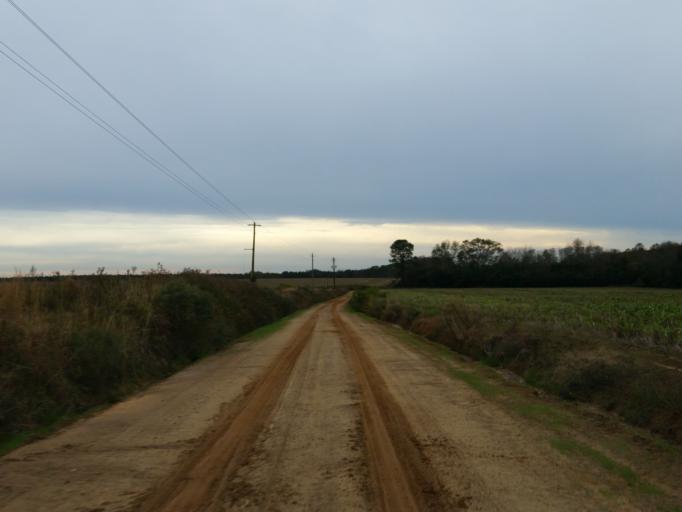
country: US
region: Georgia
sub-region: Crisp County
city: Cordele
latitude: 31.8926
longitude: -83.7168
